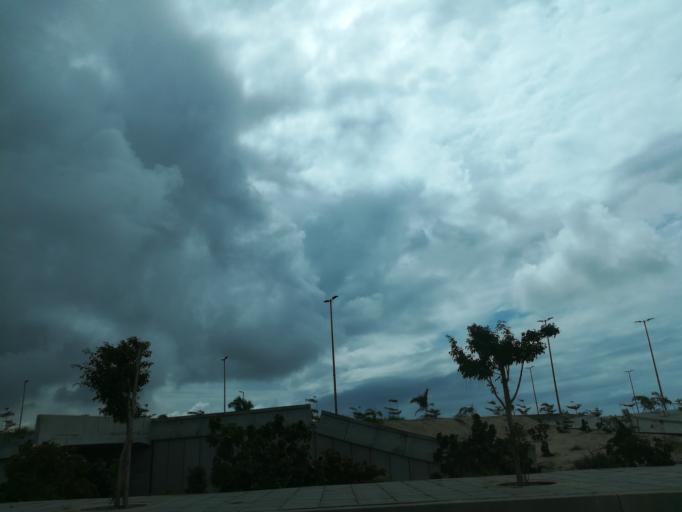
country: NG
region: Lagos
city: Lagos
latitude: 6.4190
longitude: 3.4135
